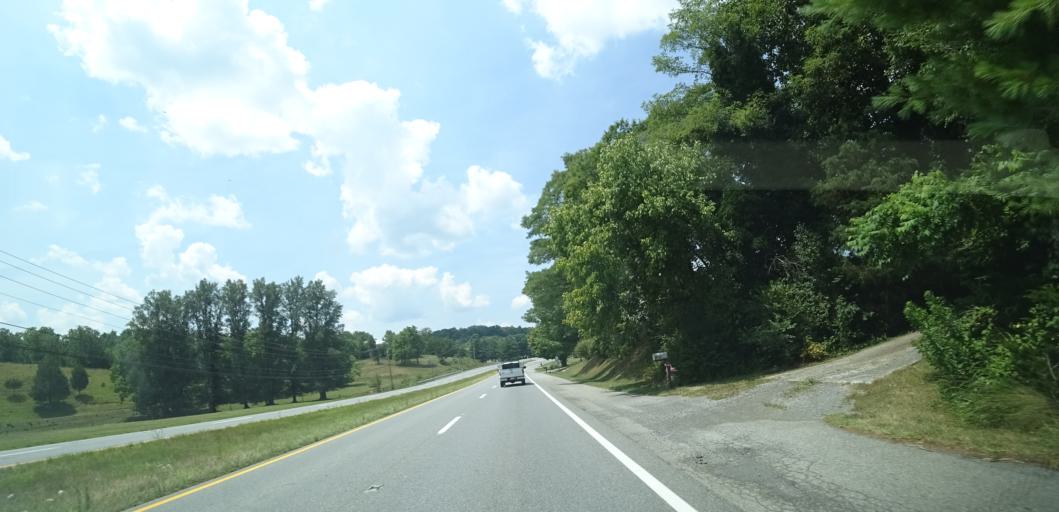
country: US
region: Virginia
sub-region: Botetourt County
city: Fincastle
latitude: 37.4573
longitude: -79.8882
